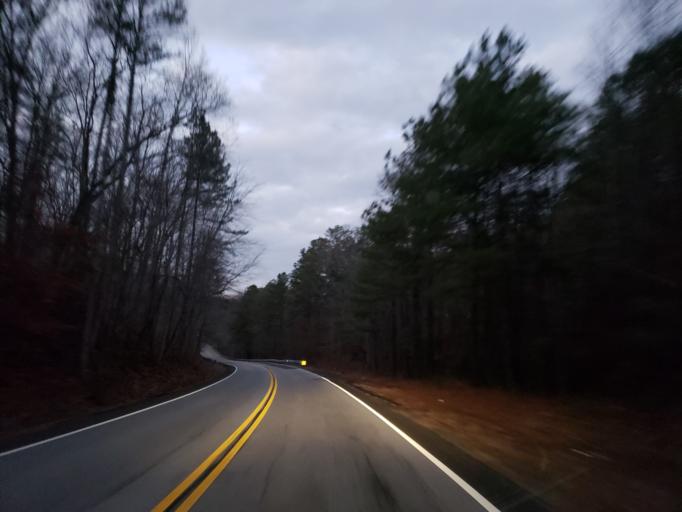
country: US
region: Georgia
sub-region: Carroll County
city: Temple
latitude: 33.7576
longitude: -85.0407
